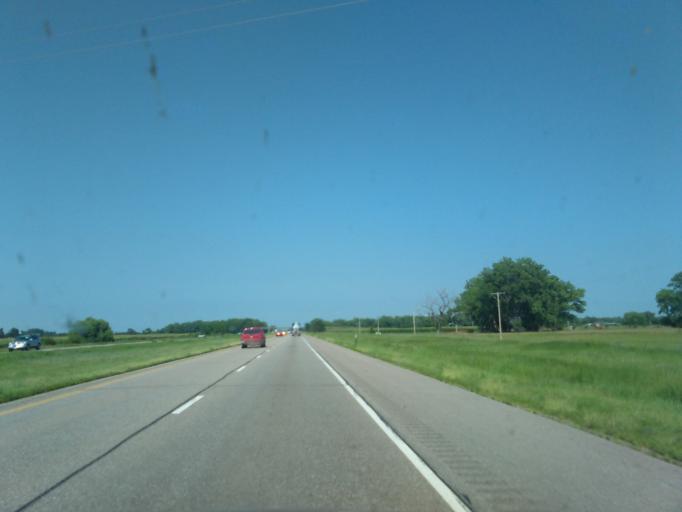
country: US
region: Nebraska
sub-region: Hall County
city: Wood River
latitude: 40.8060
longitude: -98.4654
